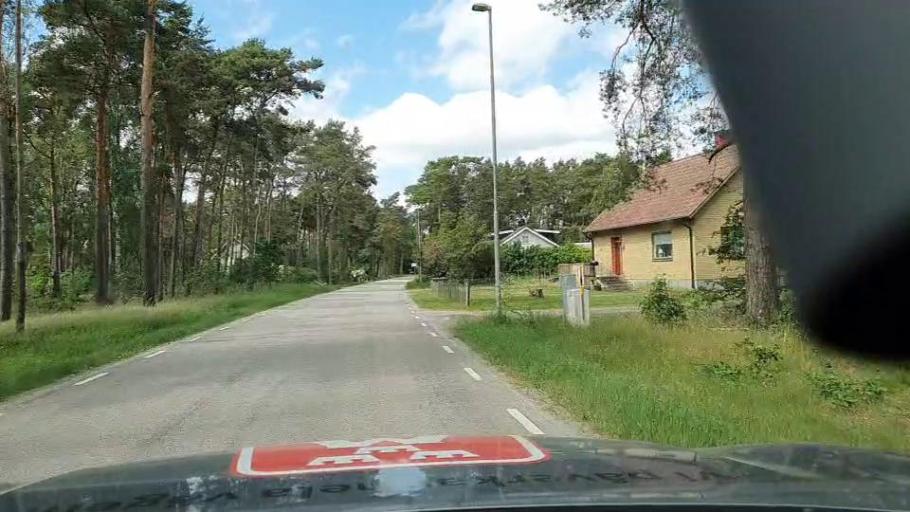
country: SE
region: Blekinge
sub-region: Karlshamns Kommun
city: Morrum
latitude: 56.0962
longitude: 14.6905
